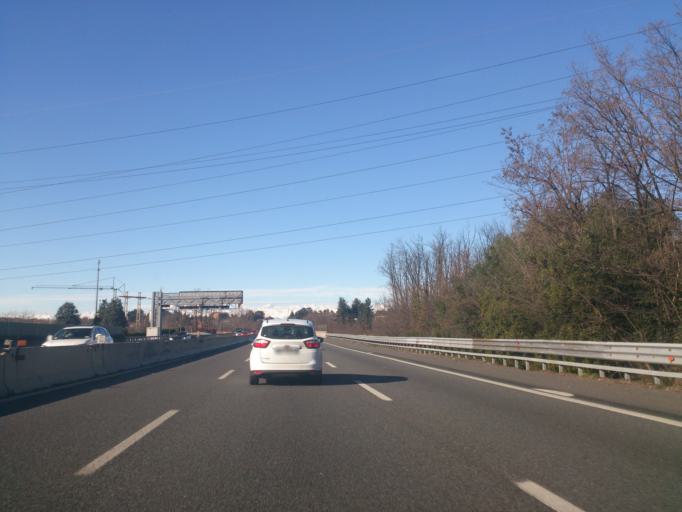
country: IT
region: Lombardy
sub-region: Provincia di Varese
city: Marnate
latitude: 45.6209
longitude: 8.9028
